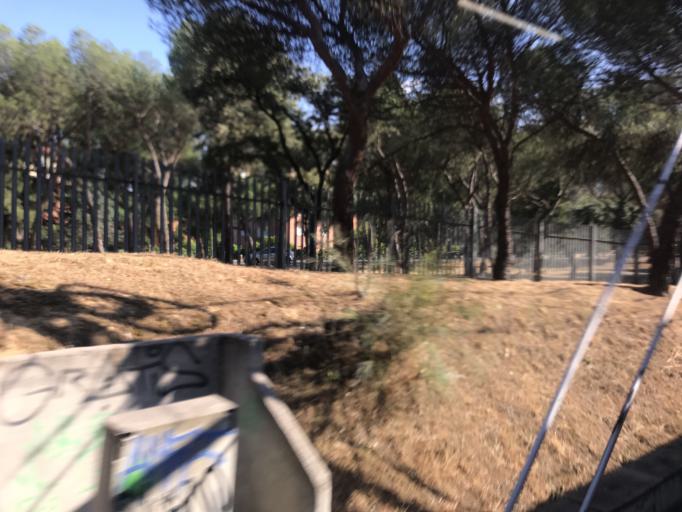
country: ES
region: Madrid
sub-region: Provincia de Madrid
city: Latina
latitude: 40.4064
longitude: -3.7560
